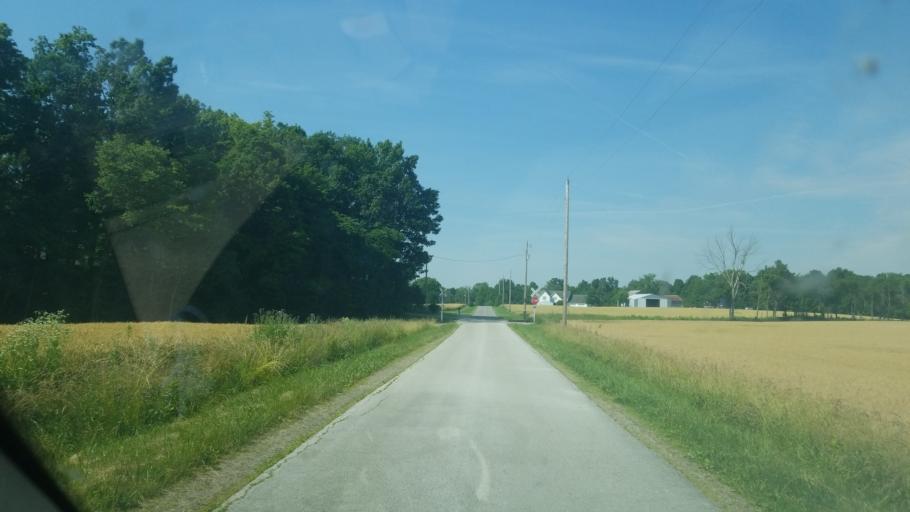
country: US
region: Ohio
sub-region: Wyandot County
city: Carey
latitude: 40.9609
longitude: -83.2802
